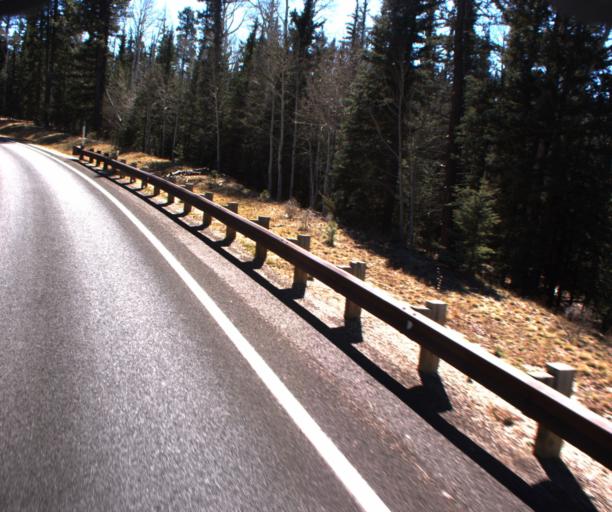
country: US
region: Arizona
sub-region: Coconino County
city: Grand Canyon
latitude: 36.5356
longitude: -112.1578
